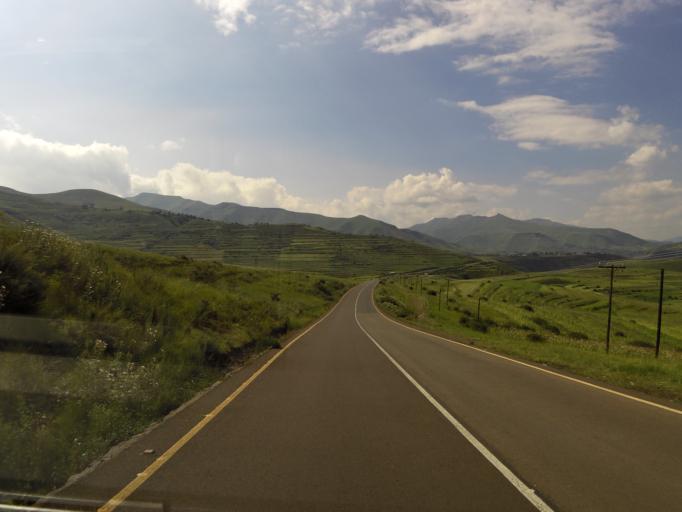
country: LS
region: Thaba-Tseka
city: Thaba-Tseka
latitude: -29.1329
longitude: 28.4933
